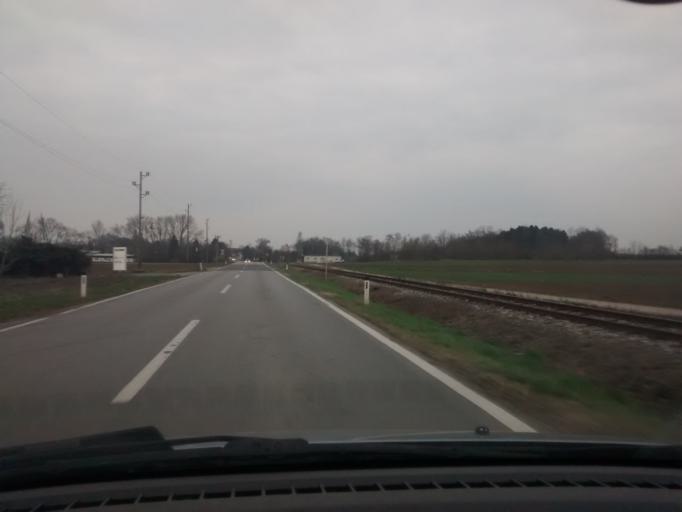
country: AT
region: Lower Austria
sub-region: Politischer Bezirk Bruck an der Leitha
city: Enzersdorf an der Fischa
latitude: 48.1003
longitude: 16.6058
